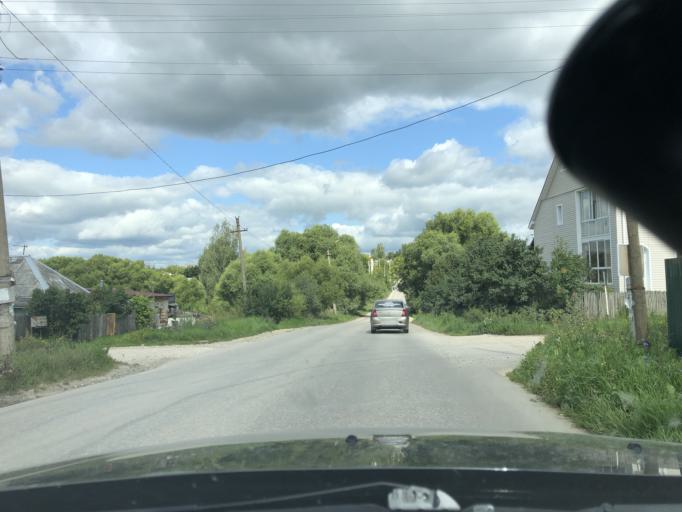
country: RU
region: Tula
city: Yasnogorsk
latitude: 54.4658
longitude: 37.7022
